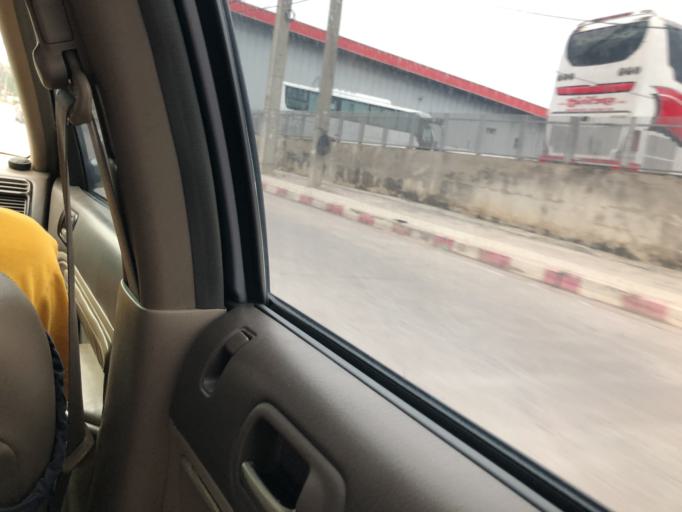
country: TH
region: Chon Buri
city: Phatthaya
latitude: 12.9491
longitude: 100.8915
